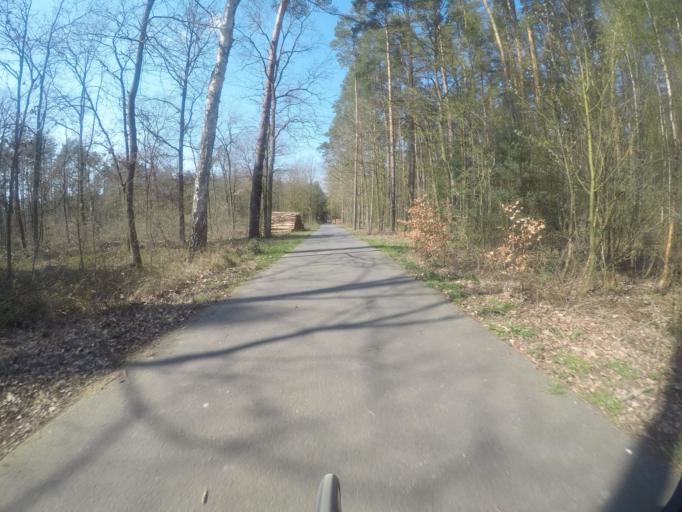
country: DE
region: Brandenburg
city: Brieselang
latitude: 52.6455
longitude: 13.0251
